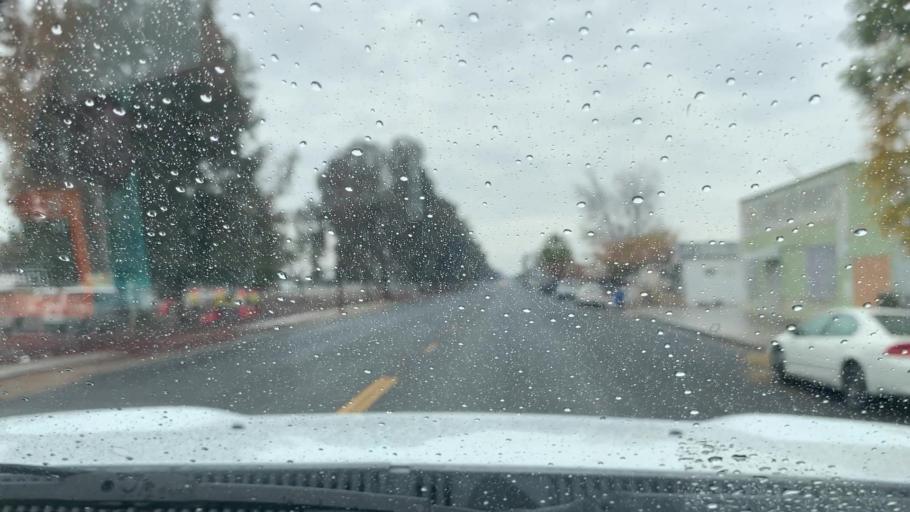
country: US
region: California
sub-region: Kern County
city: Delano
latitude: 35.7634
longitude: -119.2488
